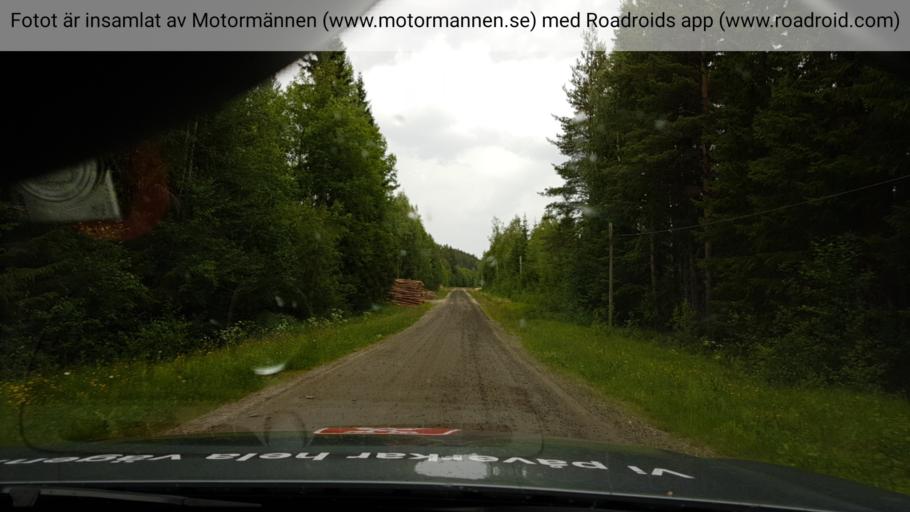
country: SE
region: Jaemtland
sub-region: Bergs Kommun
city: Hoverberg
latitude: 62.5167
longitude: 14.7073
